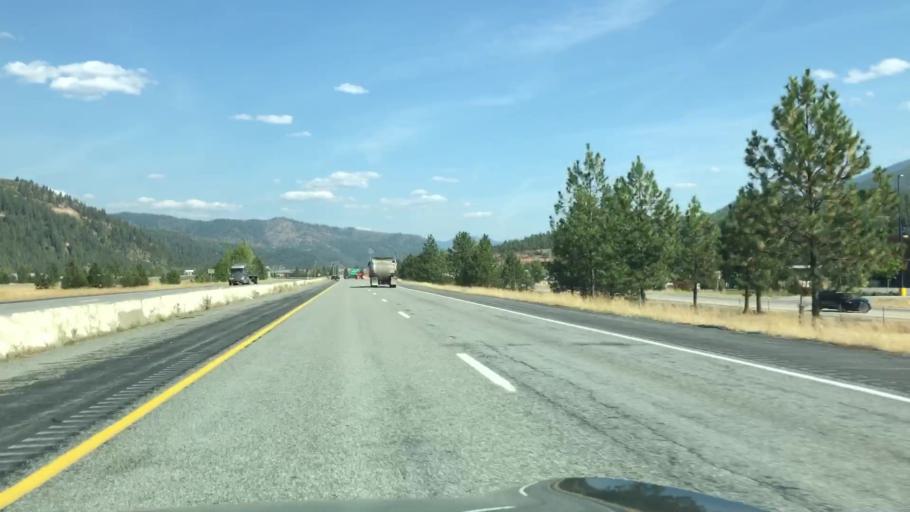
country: US
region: Idaho
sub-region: Shoshone County
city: Pinehurst
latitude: 47.5461
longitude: -116.1884
